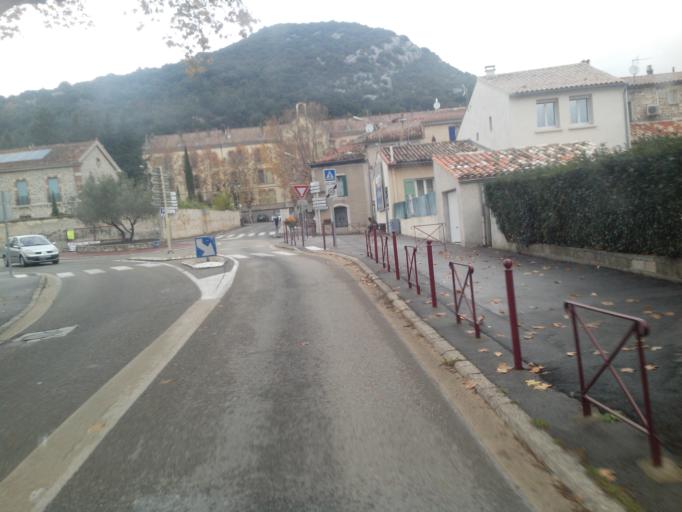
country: FR
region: Languedoc-Roussillon
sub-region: Departement du Gard
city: Saint-Hippolyte-du-Fort
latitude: 43.9638
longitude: 3.8543
